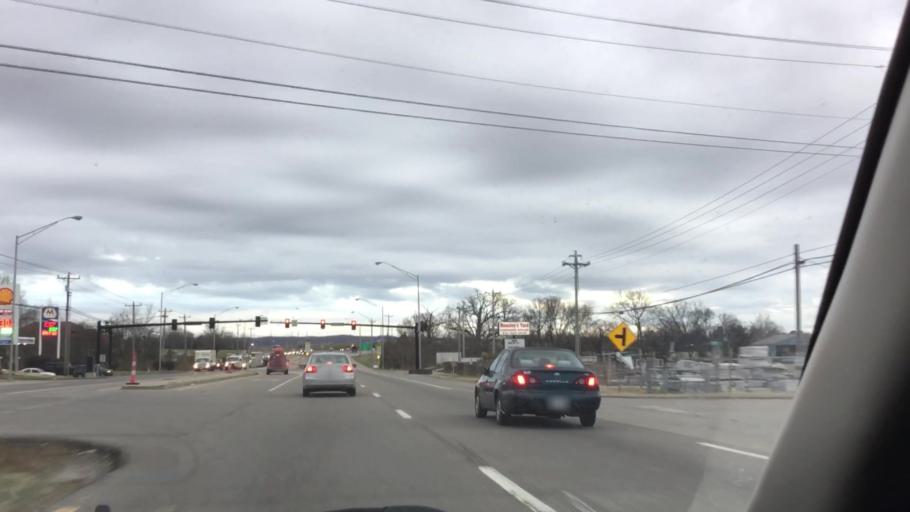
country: US
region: Tennessee
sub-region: Maury County
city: Spring Hill
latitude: 35.7109
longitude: -86.9740
